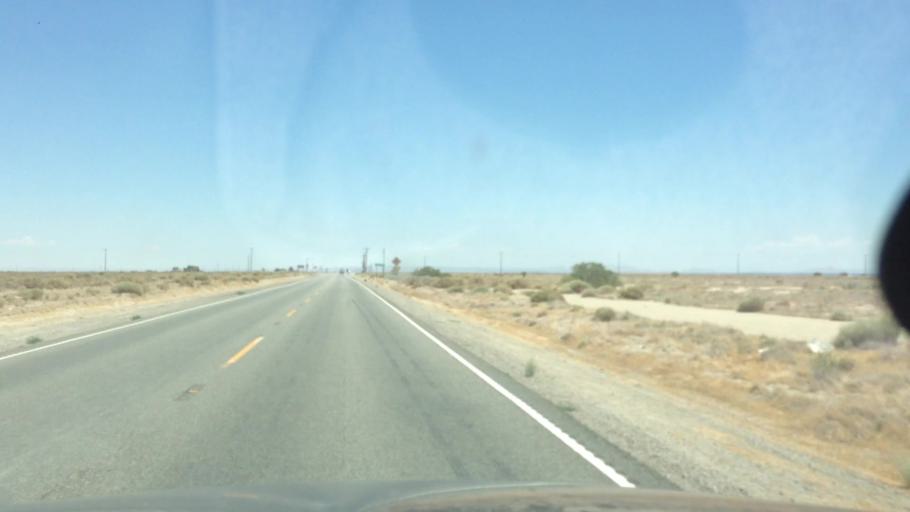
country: US
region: California
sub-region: Kern County
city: Rosamond
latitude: 34.7767
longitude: -118.2427
